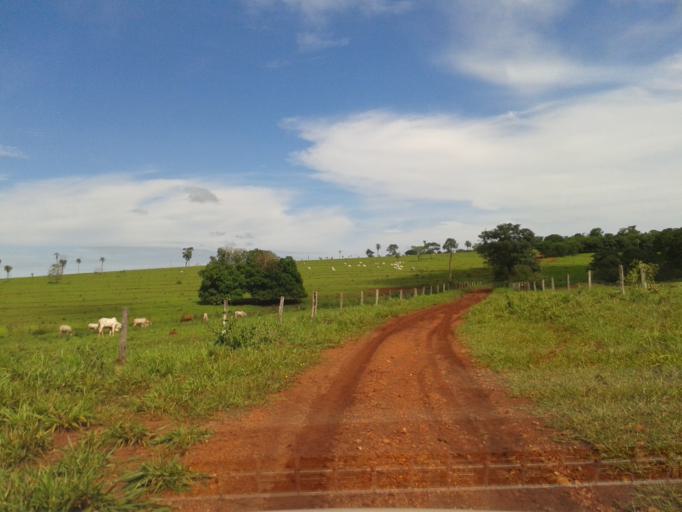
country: BR
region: Minas Gerais
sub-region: Santa Vitoria
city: Santa Vitoria
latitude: -19.2163
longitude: -50.6776
